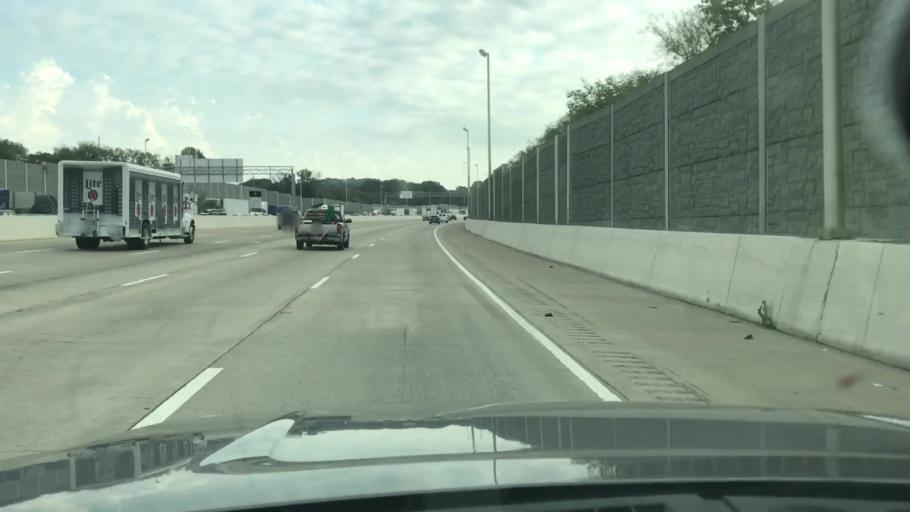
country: US
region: Tennessee
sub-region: Davidson County
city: Nashville
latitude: 36.2334
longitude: -86.7677
